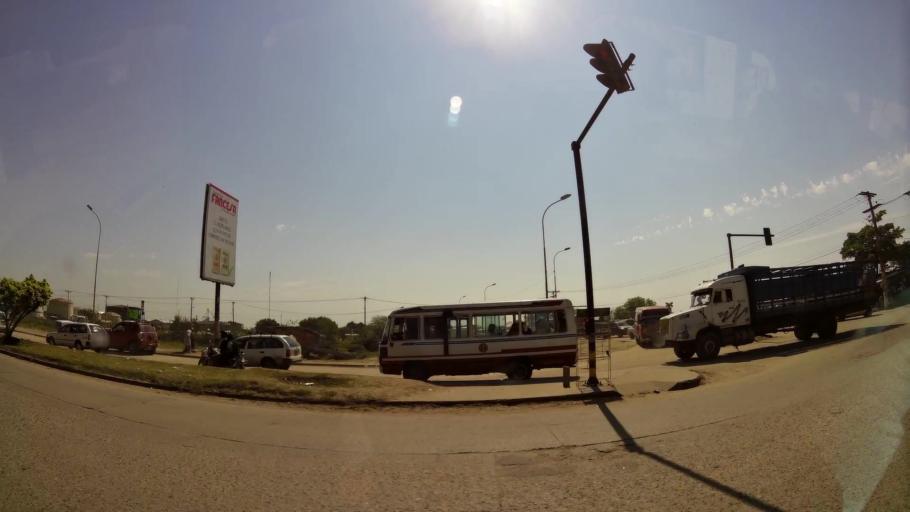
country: BO
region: Santa Cruz
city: Santa Cruz de la Sierra
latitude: -17.7521
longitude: -63.1292
